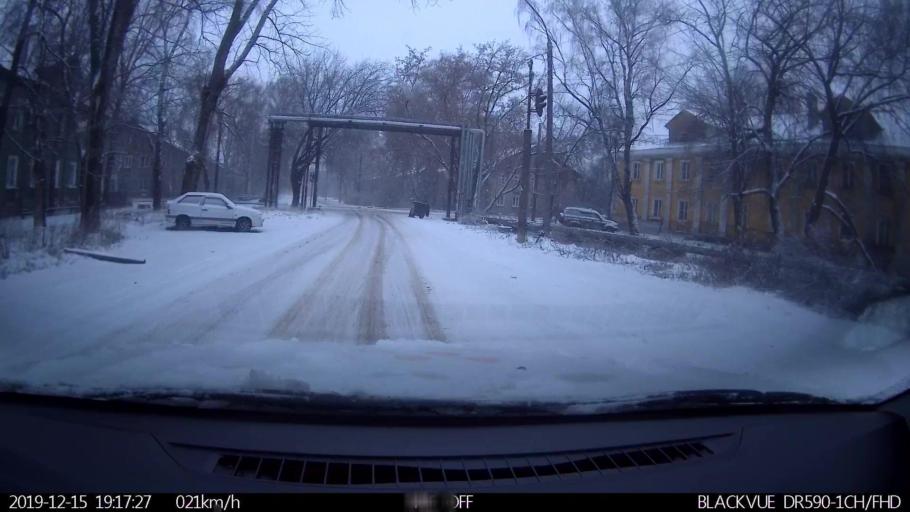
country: RU
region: Nizjnij Novgorod
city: Gorbatovka
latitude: 56.3506
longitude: 43.8445
